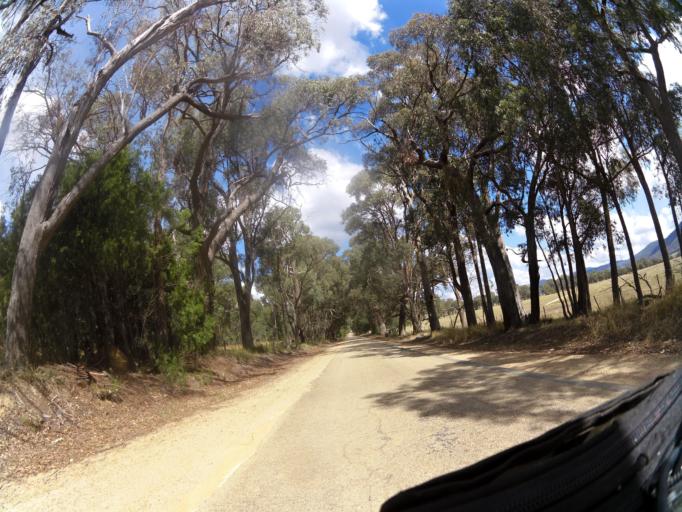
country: AU
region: Victoria
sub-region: Benalla
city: Benalla
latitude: -36.7741
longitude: 145.9743
